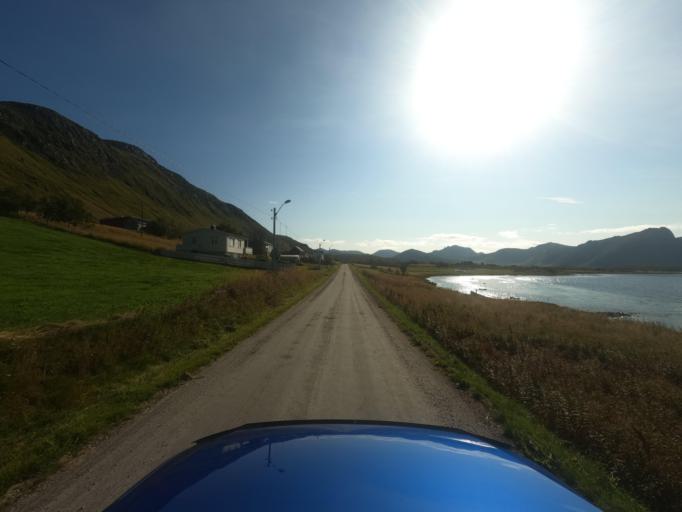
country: NO
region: Nordland
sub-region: Vestvagoy
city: Evjen
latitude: 68.2704
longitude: 13.7956
